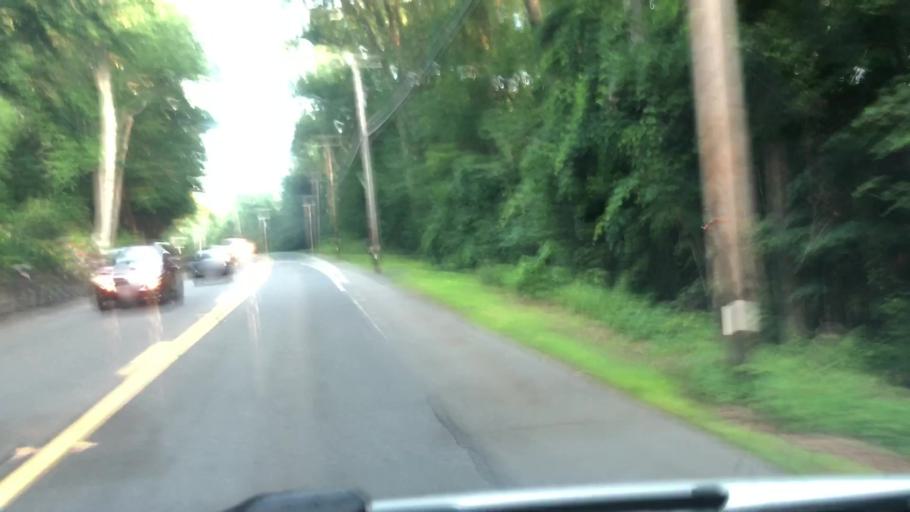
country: US
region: Massachusetts
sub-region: Hampshire County
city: Williamsburg
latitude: 42.4174
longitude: -72.7690
